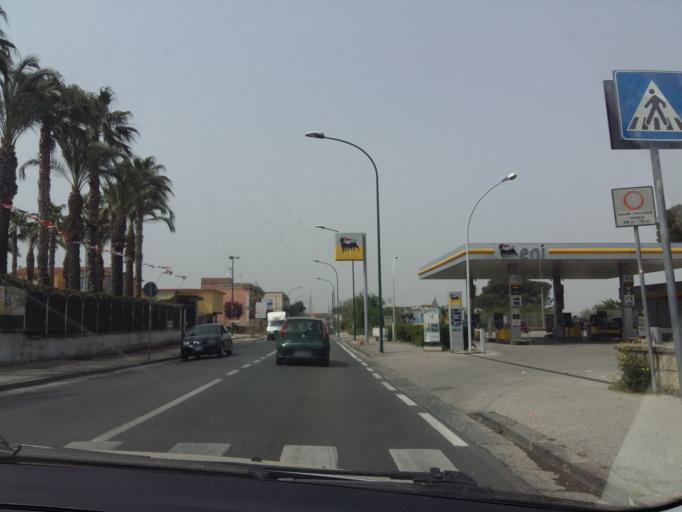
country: IT
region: Campania
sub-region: Provincia di Napoli
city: Mugnano di Napoli
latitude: 40.8955
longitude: 14.2149
